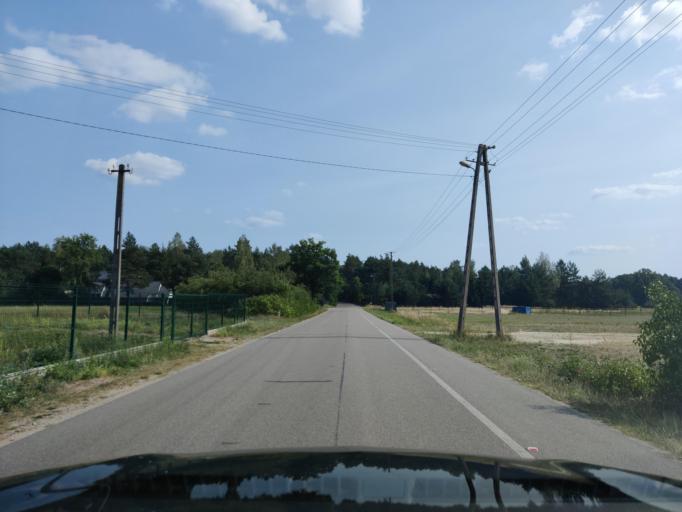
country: PL
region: Masovian Voivodeship
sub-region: Powiat makowski
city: Rozan
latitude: 52.8730
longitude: 21.4315
